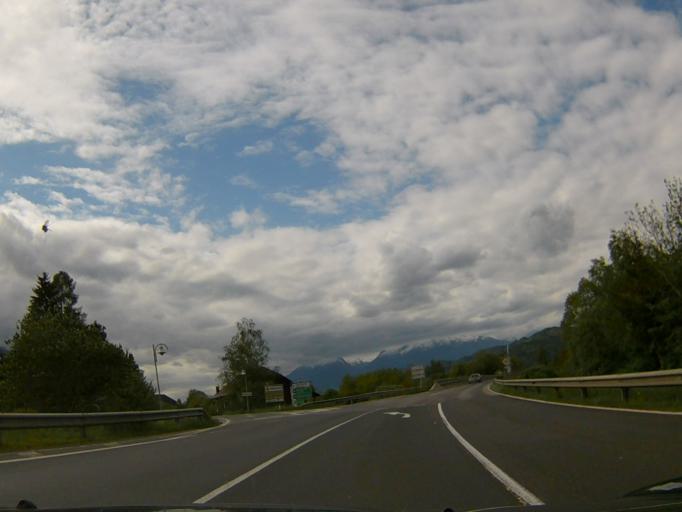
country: AT
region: Carinthia
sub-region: Politischer Bezirk Villach Land
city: Ferndorf
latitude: 46.7425
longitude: 13.5888
